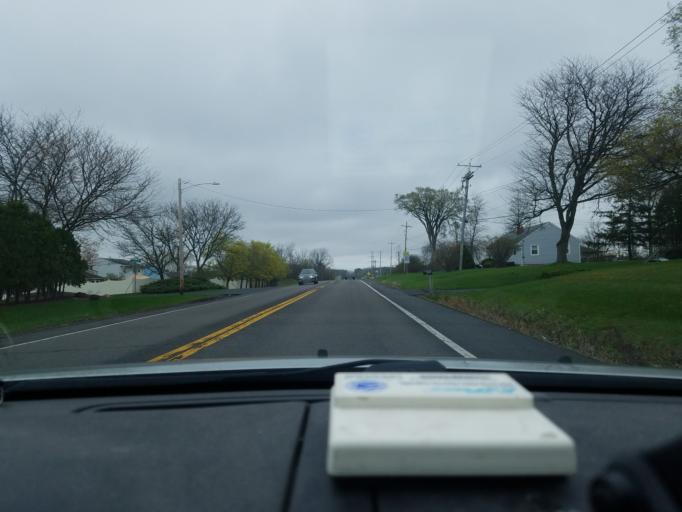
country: US
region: New York
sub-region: Onondaga County
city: North Syracuse
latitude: 43.1588
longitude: -76.1000
